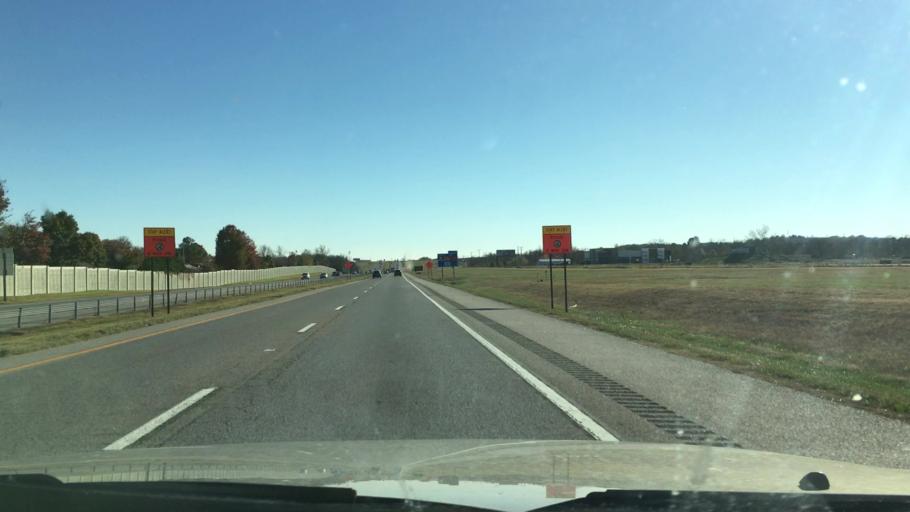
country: US
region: Oklahoma
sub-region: Tulsa County
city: Glenpool
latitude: 36.0005
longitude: -96.0118
